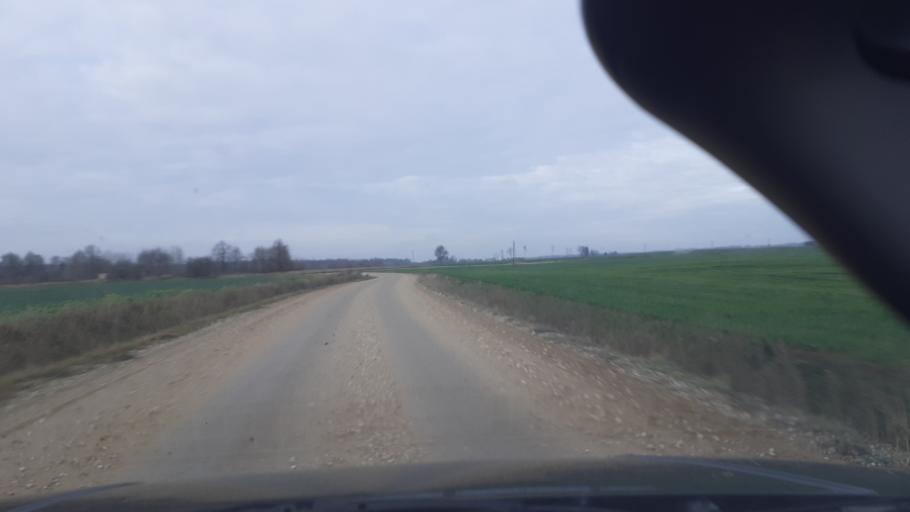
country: LV
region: Aizpute
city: Aizpute
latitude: 56.8543
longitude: 21.6685
